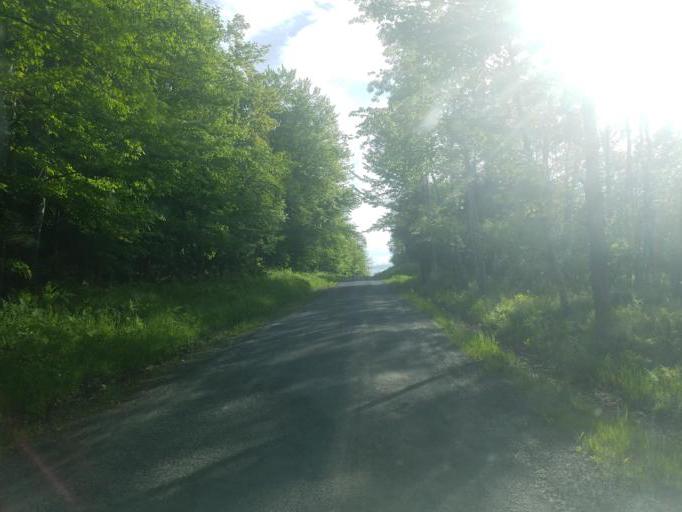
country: US
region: New York
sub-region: Herkimer County
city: Dolgeville
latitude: 43.3390
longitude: -74.9277
